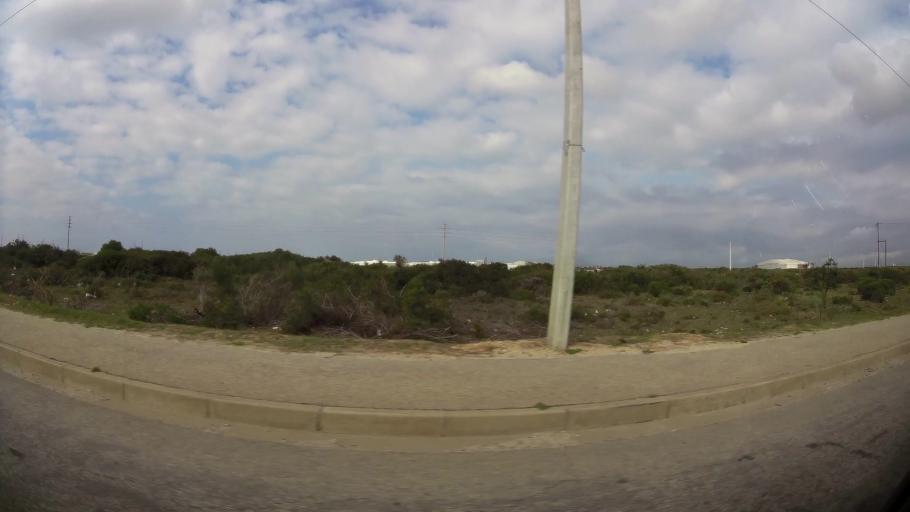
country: ZA
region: Eastern Cape
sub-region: Nelson Mandela Bay Metropolitan Municipality
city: Port Elizabeth
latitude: -33.8080
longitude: 25.6183
